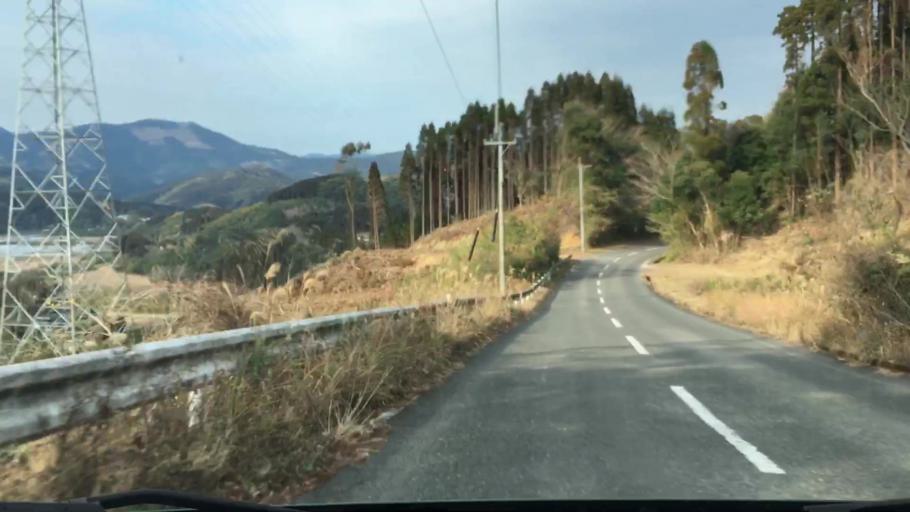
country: JP
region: Miyazaki
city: Nichinan
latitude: 31.6087
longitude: 131.3297
